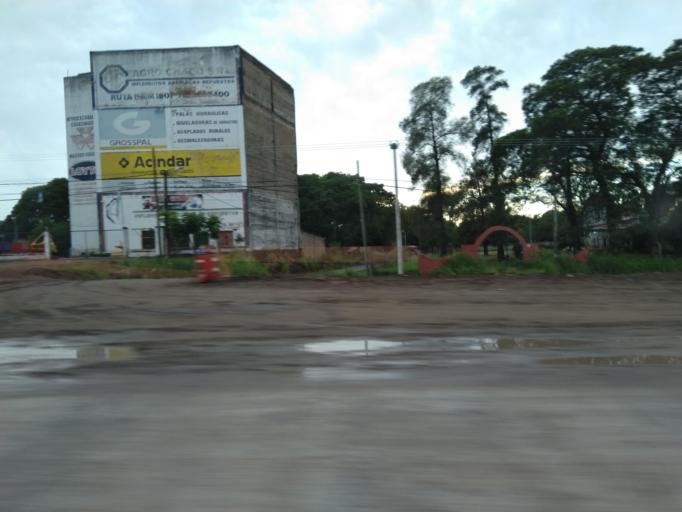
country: AR
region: Chaco
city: Fontana
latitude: -27.4185
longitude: -59.0051
